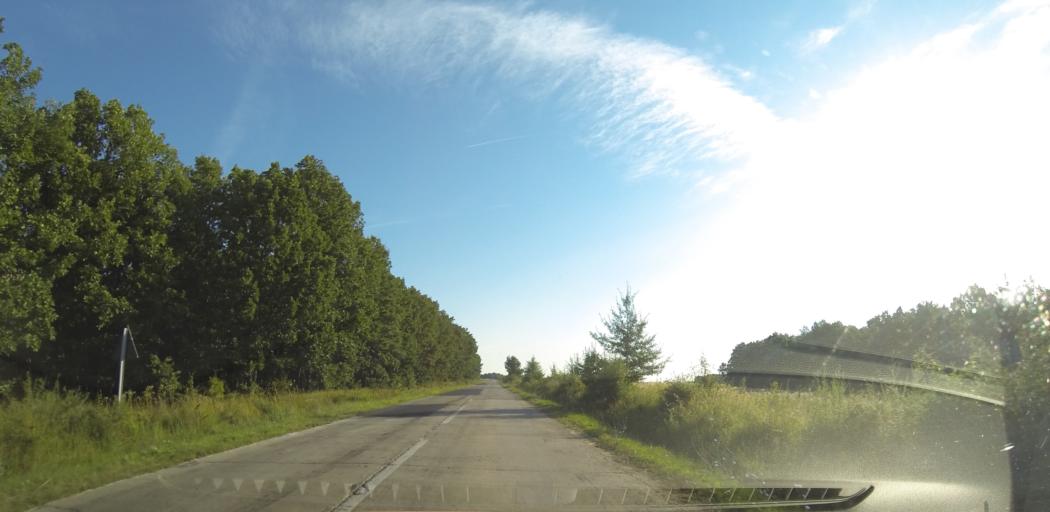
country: RO
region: Valcea
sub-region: Comuna Balcesti
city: Balcesti
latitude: 44.5980
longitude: 23.9270
